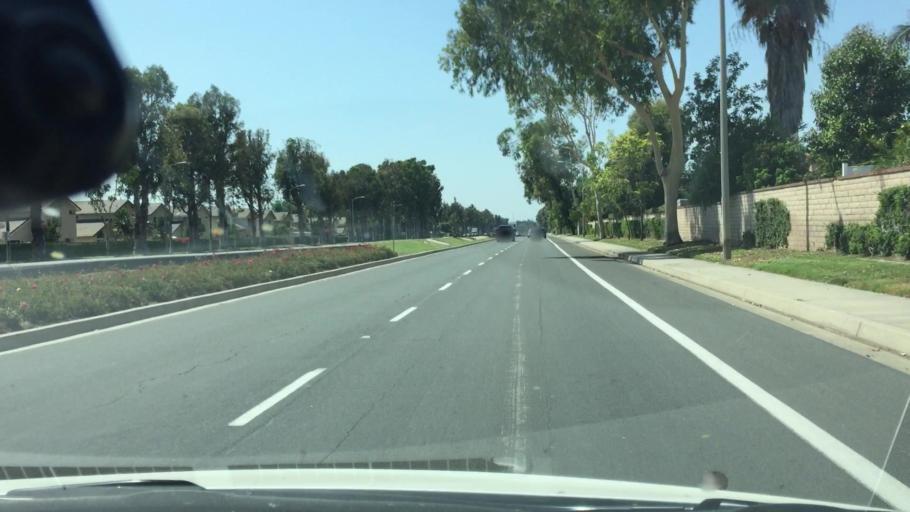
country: US
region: California
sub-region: Orange County
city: Irvine
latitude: 33.7015
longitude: -117.7689
